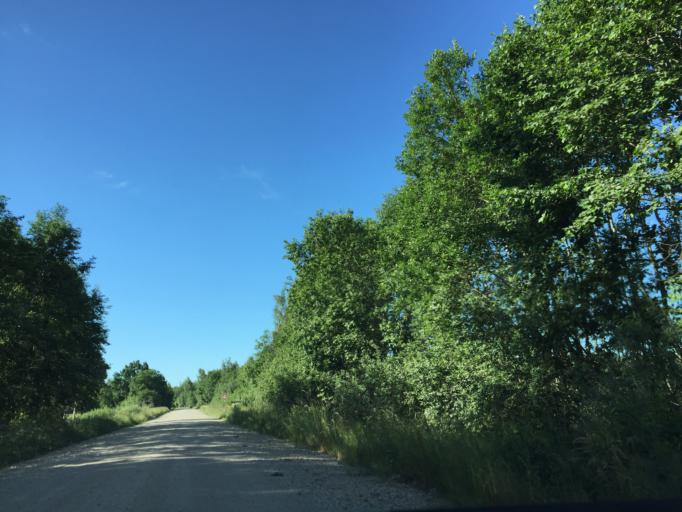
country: LV
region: Ventspils Rajons
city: Piltene
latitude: 57.3195
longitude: 21.6895
